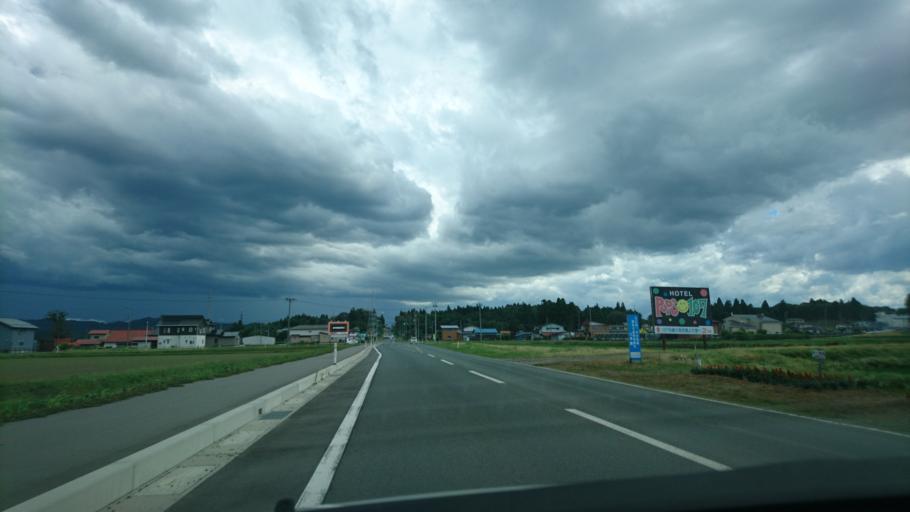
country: JP
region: Iwate
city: Kitakami
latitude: 39.3147
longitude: 141.1268
